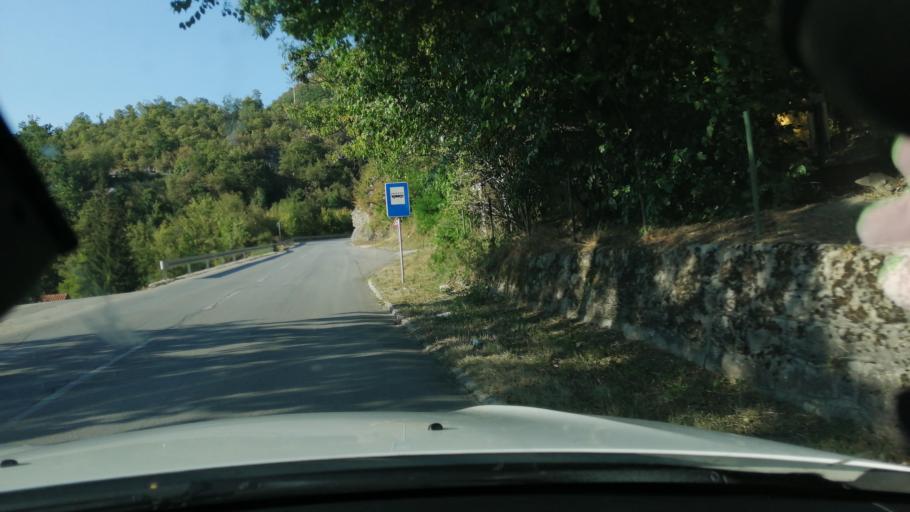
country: RS
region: Central Serbia
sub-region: Moravicki Okrug
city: Ivanjica
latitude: 43.6334
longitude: 20.2435
